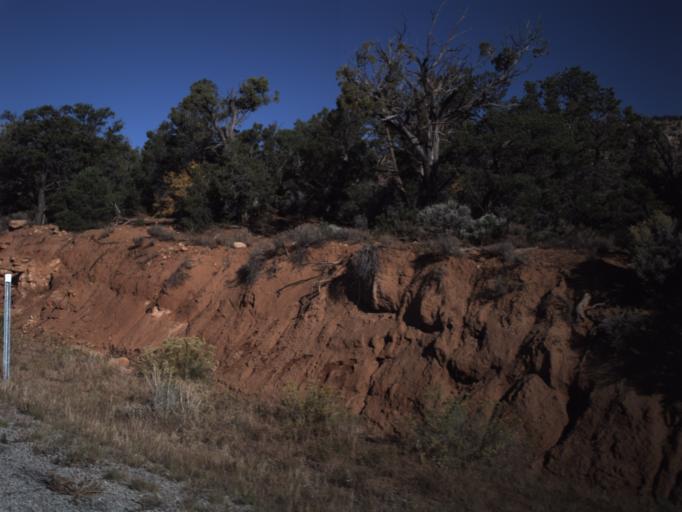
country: US
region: Utah
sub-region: San Juan County
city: Blanding
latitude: 37.5867
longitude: -109.8973
